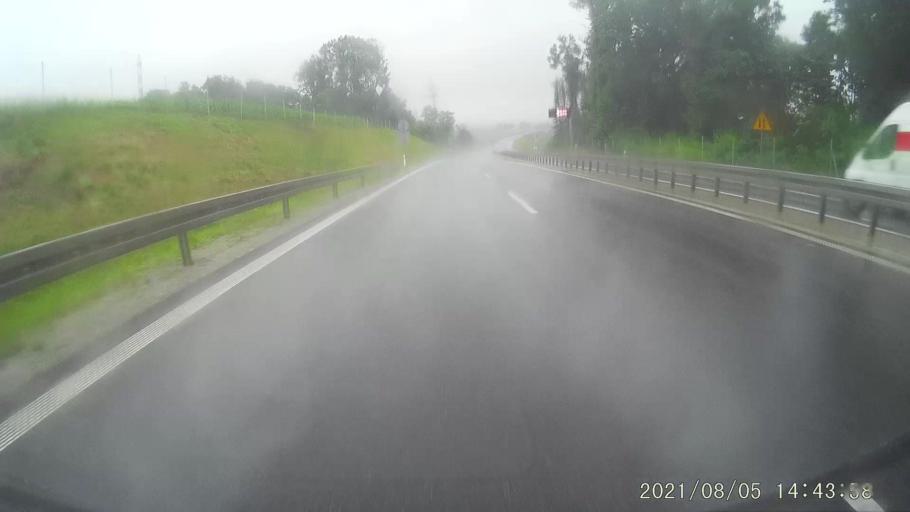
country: PL
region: Opole Voivodeship
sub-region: Powiat nyski
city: Nysa
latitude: 50.4899
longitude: 17.3855
